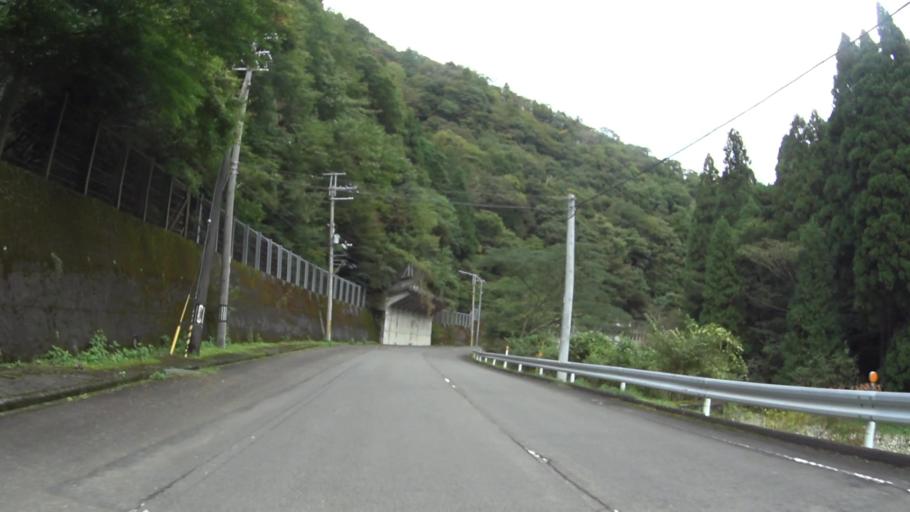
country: JP
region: Fukui
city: Obama
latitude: 35.2839
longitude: 135.6962
